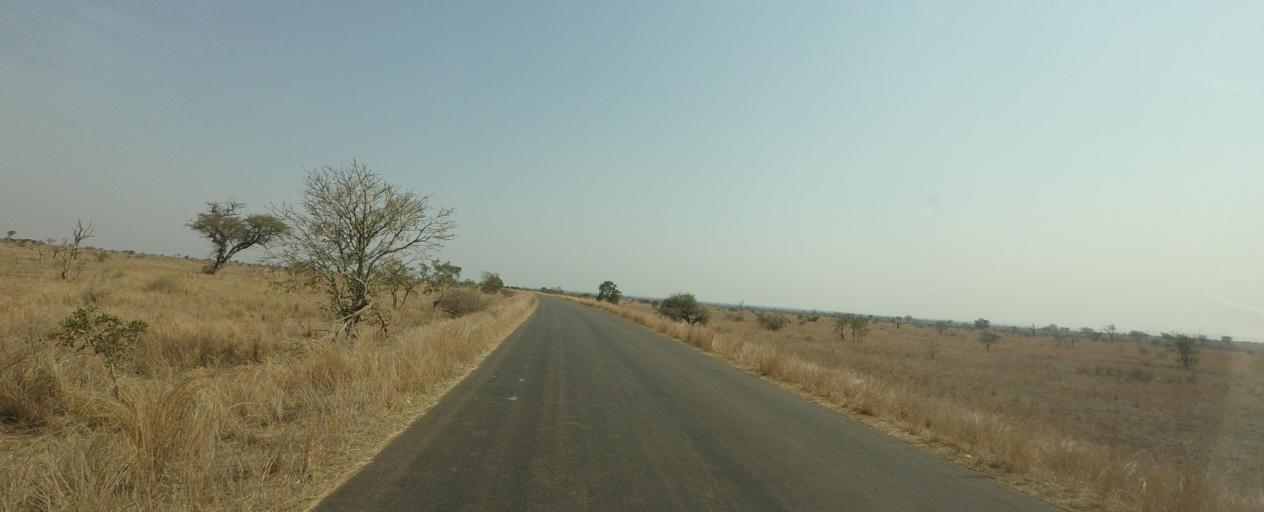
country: ZA
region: Limpopo
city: Thulamahashi
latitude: -24.3301
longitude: 31.7559
